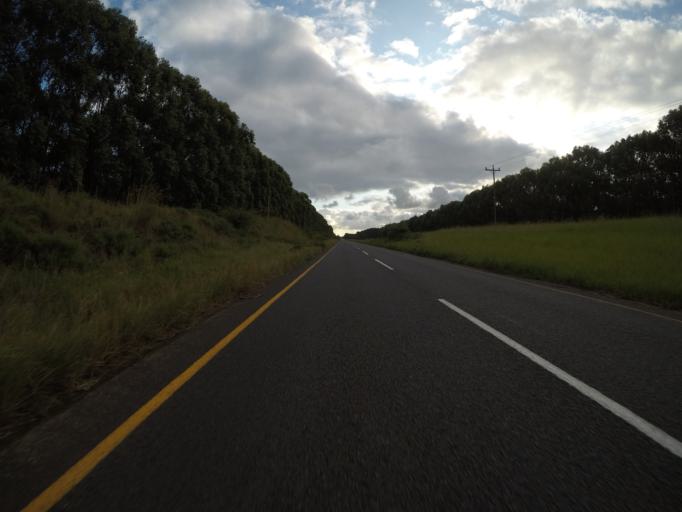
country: ZA
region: KwaZulu-Natal
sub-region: uMkhanyakude District Municipality
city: Mtubatuba
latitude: -28.3914
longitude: 32.2261
